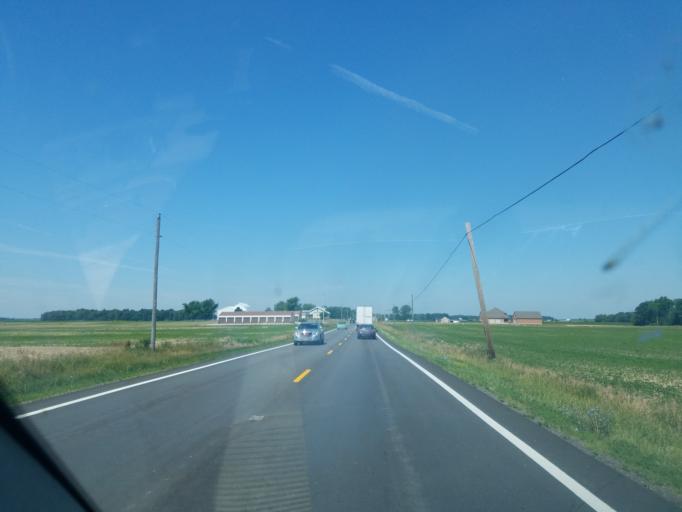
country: US
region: Ohio
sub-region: Shelby County
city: Jackson Center
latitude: 40.4396
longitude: -84.0717
